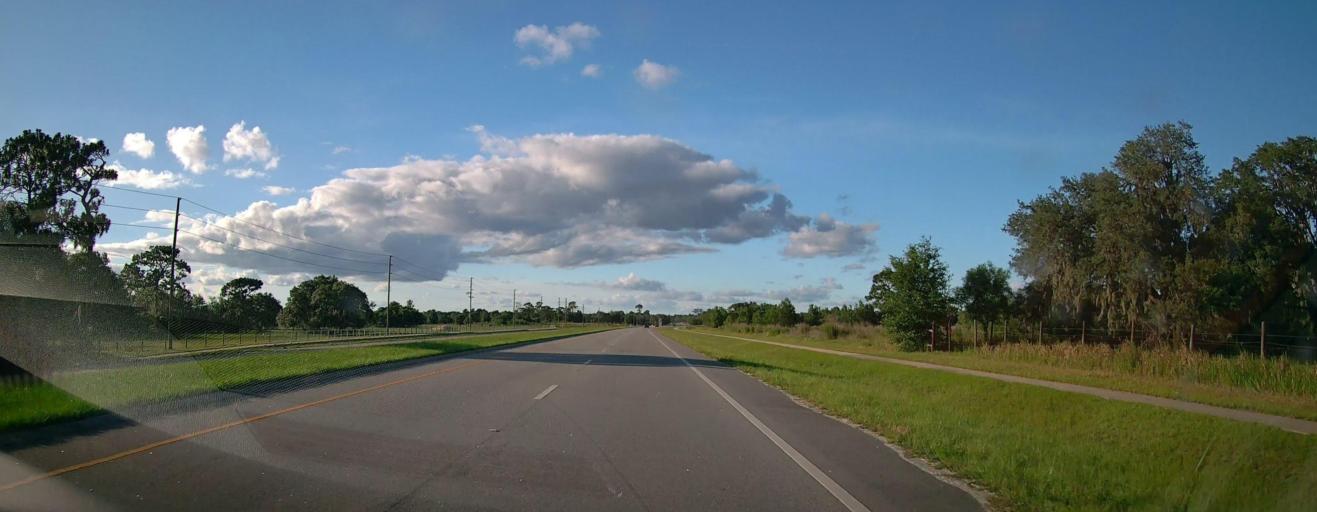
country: US
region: Florida
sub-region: Marion County
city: Belleview
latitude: 29.0471
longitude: -82.0174
